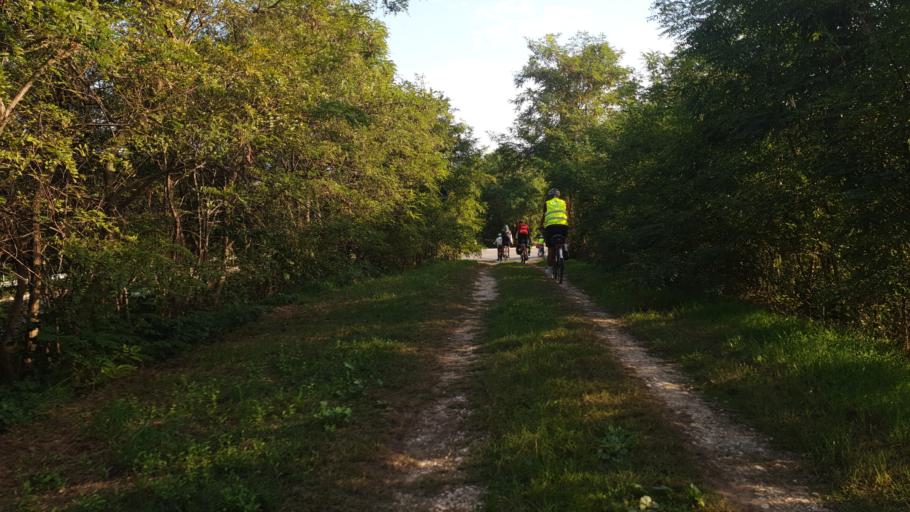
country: IT
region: Veneto
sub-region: Provincia di Padova
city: Montagnana
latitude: 45.2521
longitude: 11.4809
